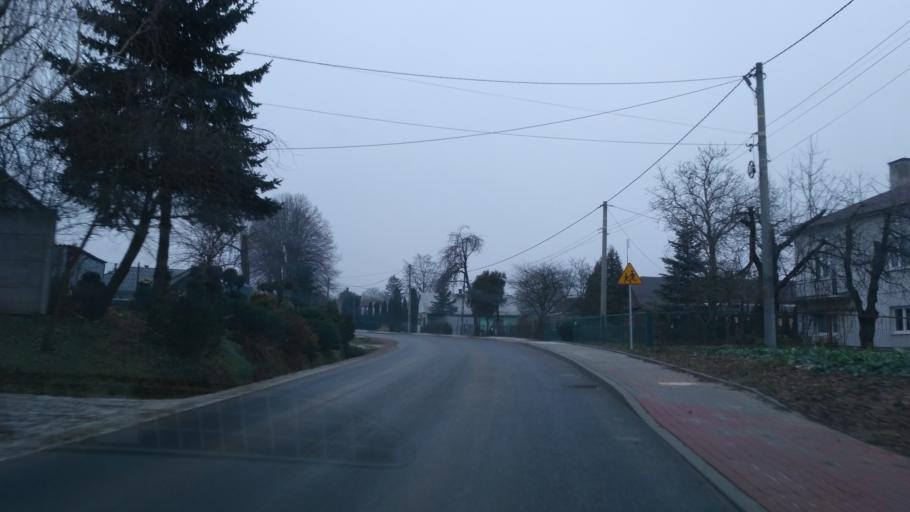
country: PL
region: Subcarpathian Voivodeship
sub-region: Powiat przeworski
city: Kanczuga
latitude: 50.0157
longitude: 22.4141
